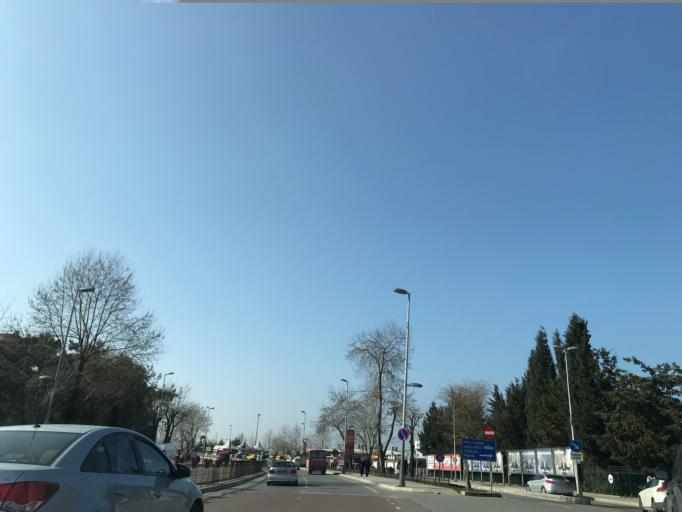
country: TR
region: Yalova
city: Yalova
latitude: 40.6586
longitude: 29.2810
